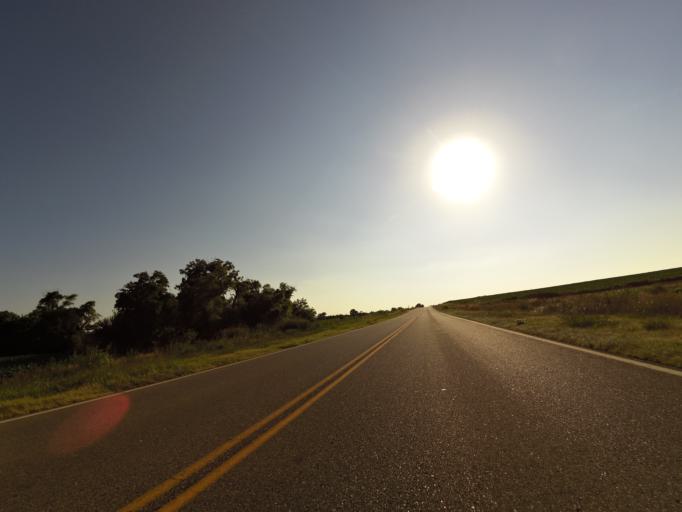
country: US
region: Kansas
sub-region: Reno County
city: Buhler
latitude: 38.1446
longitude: -97.8107
